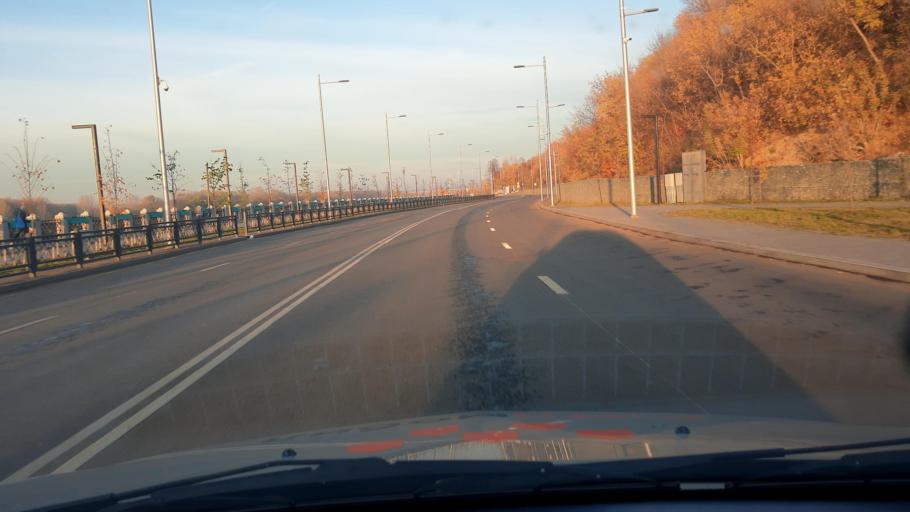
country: RU
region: Bashkortostan
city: Ufa
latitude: 54.7126
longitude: 55.9467
